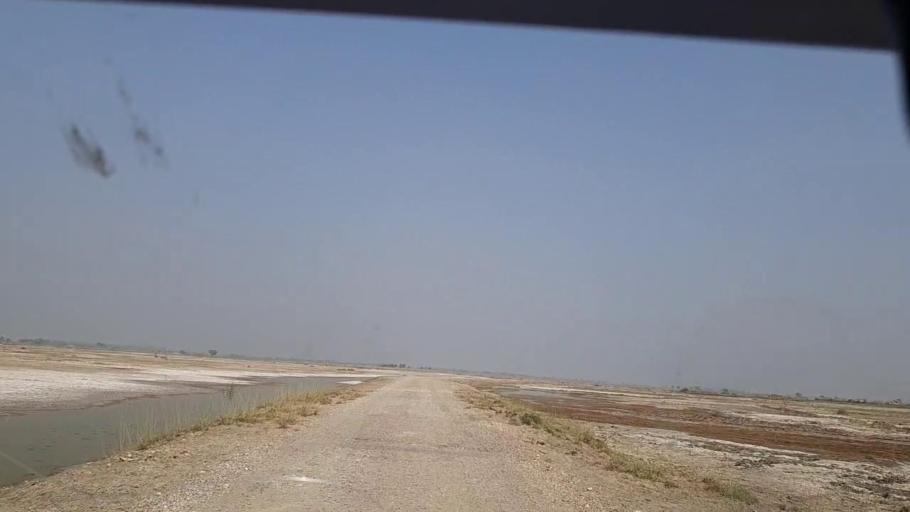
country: PK
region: Sindh
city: Shikarpur
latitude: 28.0476
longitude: 68.6538
